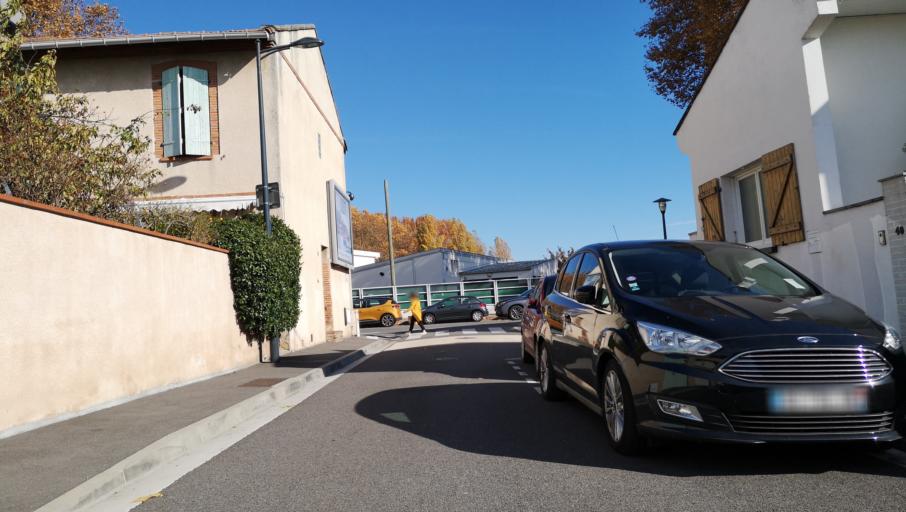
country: FR
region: Midi-Pyrenees
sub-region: Departement de la Haute-Garonne
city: Blagnac
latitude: 43.6162
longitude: 1.4086
